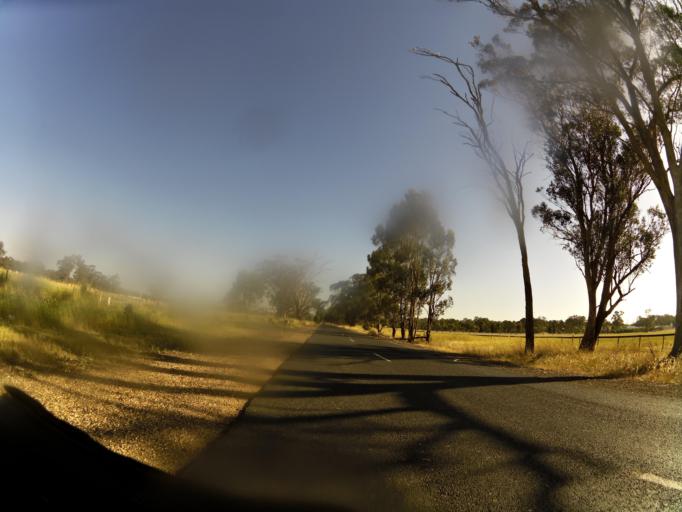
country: AU
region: Victoria
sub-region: Murrindindi
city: Kinglake West
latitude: -36.9817
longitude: 145.1109
